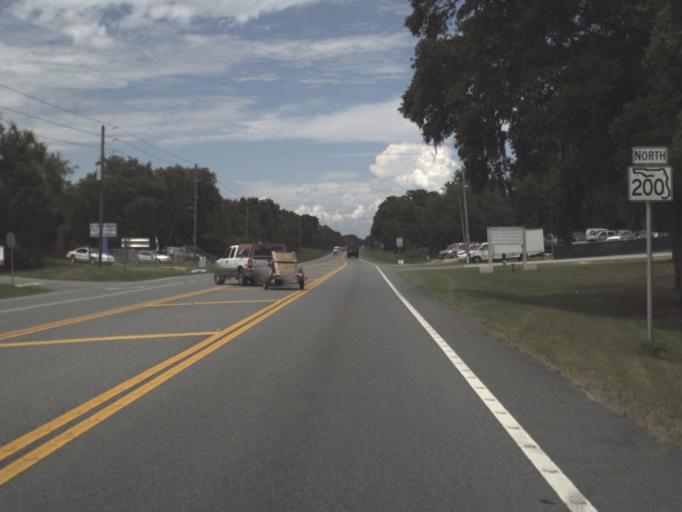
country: US
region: Florida
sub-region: Citrus County
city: Hernando
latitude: 28.9760
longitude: -82.3624
